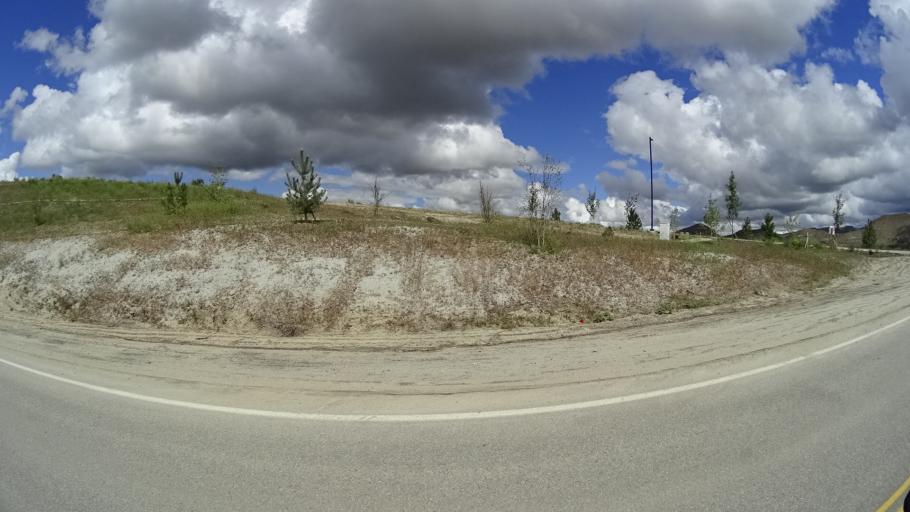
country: US
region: Idaho
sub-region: Ada County
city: Boise
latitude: 43.6641
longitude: -116.1920
